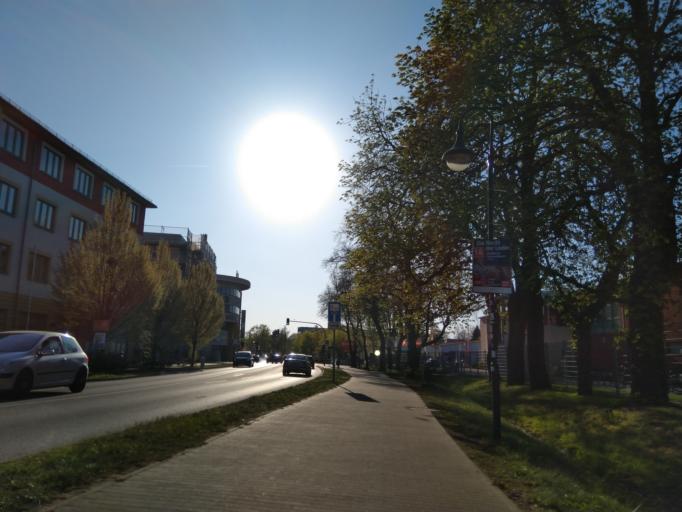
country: DE
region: Brandenburg
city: Bernau bei Berlin
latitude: 52.6749
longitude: 13.5754
